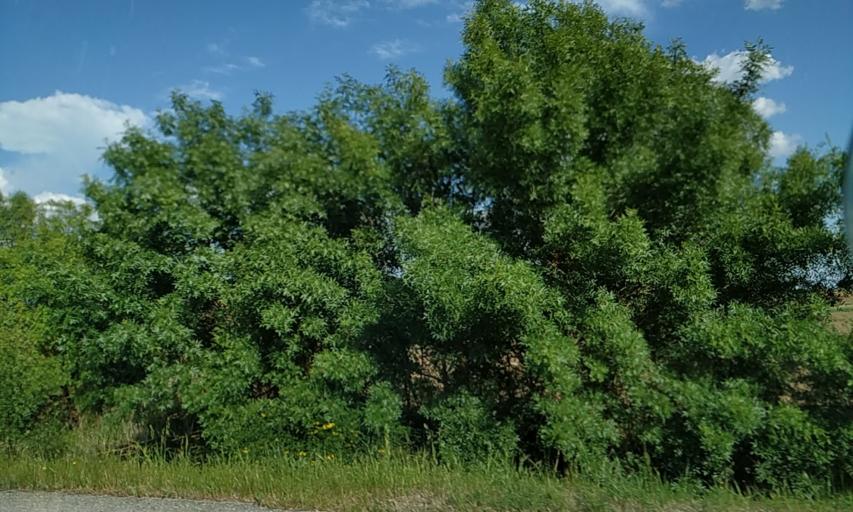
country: PT
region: Evora
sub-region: Estremoz
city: Estremoz
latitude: 38.9798
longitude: -7.4846
